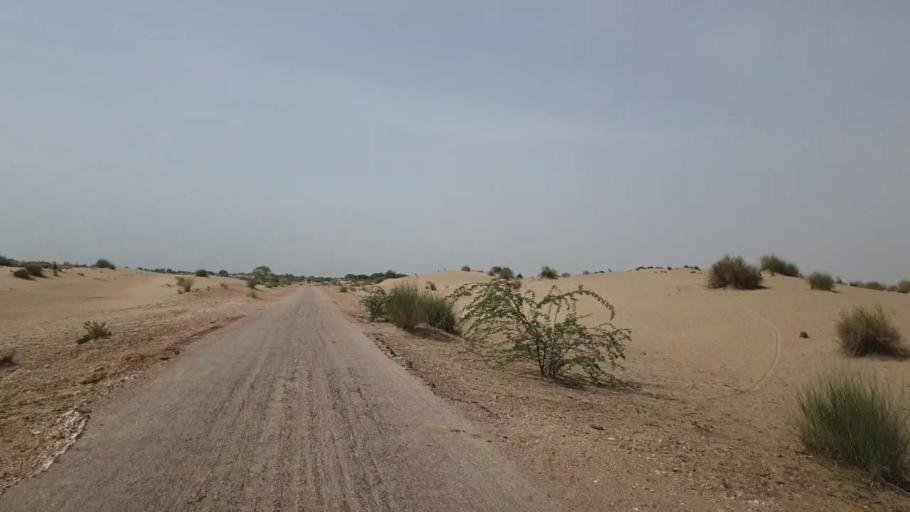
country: PK
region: Sindh
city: Bandhi
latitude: 26.5417
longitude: 68.3862
